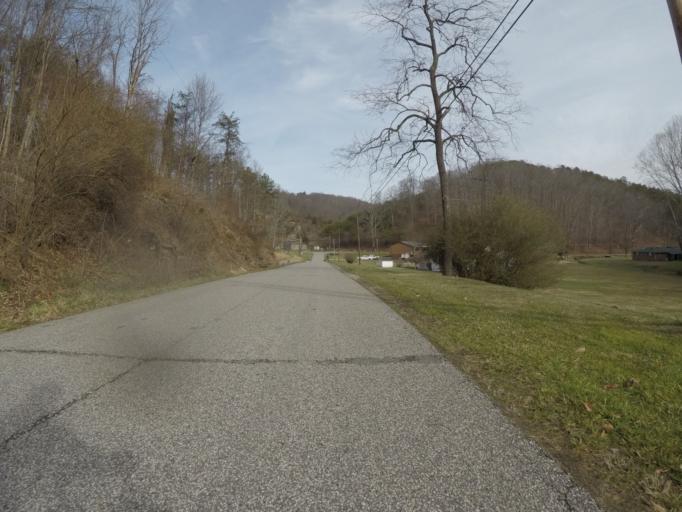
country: US
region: West Virginia
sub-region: Cabell County
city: Pea Ridge
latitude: 38.3577
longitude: -82.3720
